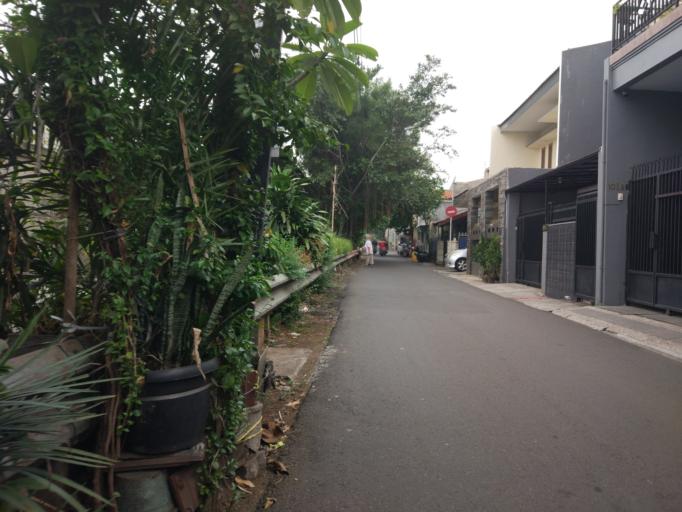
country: ID
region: Jakarta Raya
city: Jakarta
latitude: -6.2407
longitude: 106.8585
